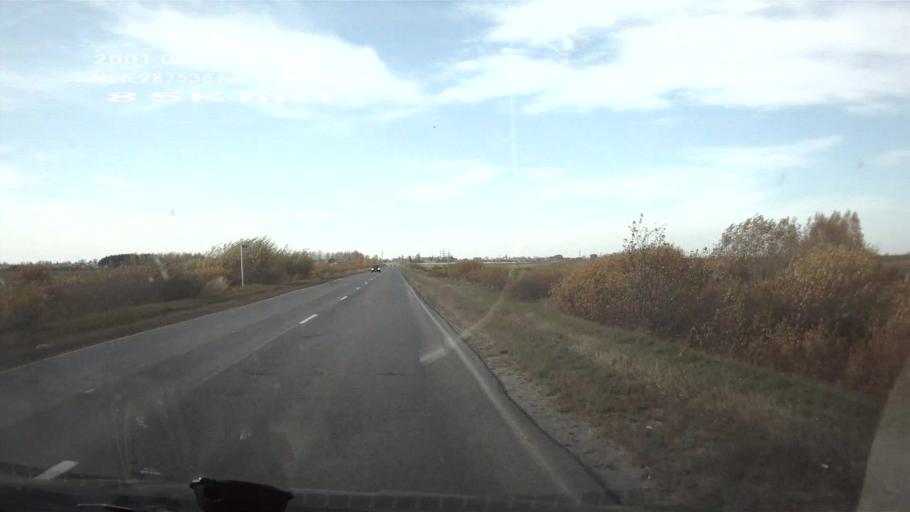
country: RU
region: Chuvashia
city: Ibresi
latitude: 55.2876
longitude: 47.0741
